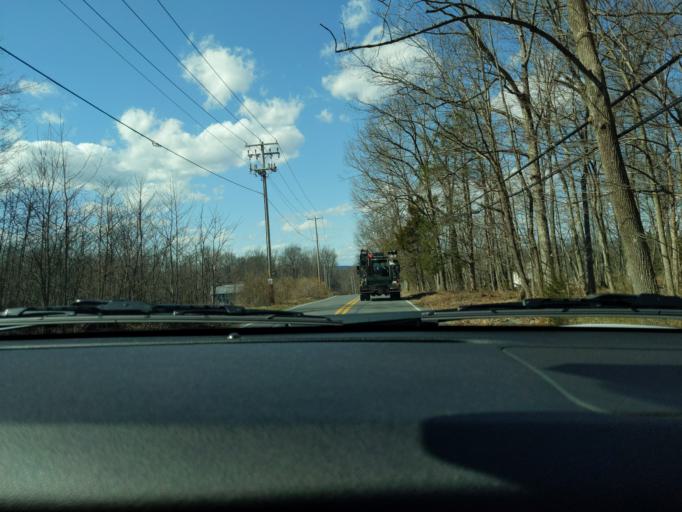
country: US
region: Pennsylvania
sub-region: Bucks County
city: Richlandtown
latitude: 40.4576
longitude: -75.2648
